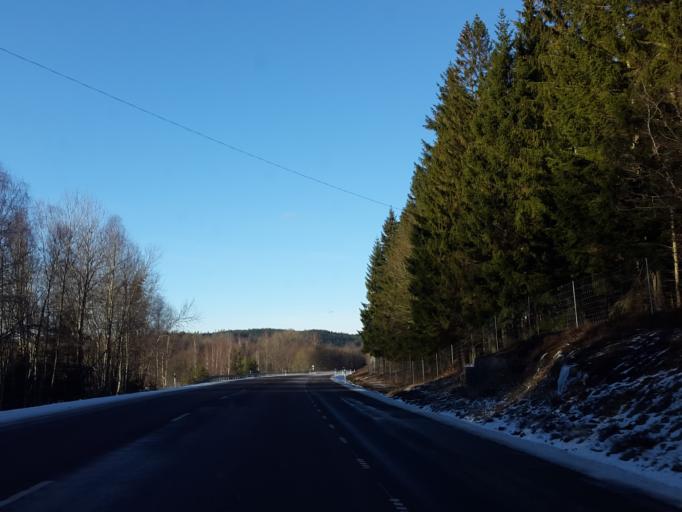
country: SE
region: Vaestra Goetaland
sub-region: Alingsas Kommun
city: Alingsas
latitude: 57.8867
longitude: 12.5547
